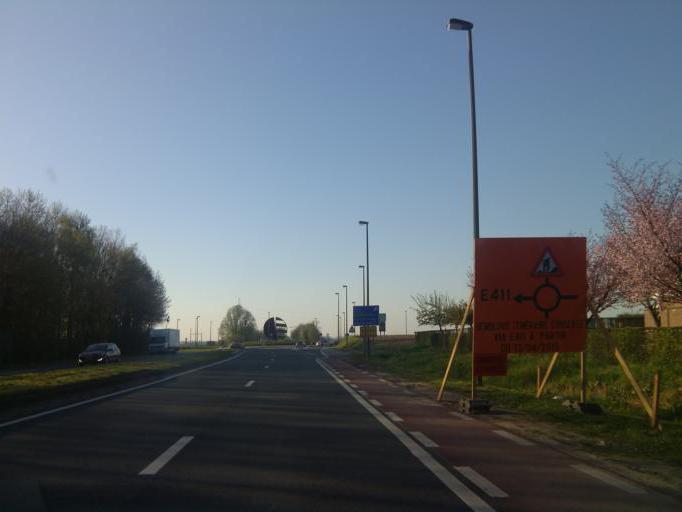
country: BE
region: Wallonia
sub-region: Province du Brabant Wallon
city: Louvain-la-Neuve
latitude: 50.6601
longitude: 4.6337
